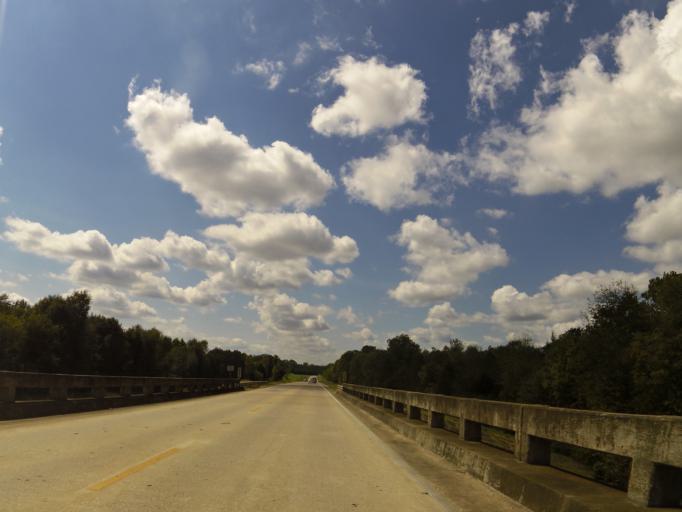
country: US
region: Alabama
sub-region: Dallas County
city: Selma
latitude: 32.3596
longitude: -87.1346
